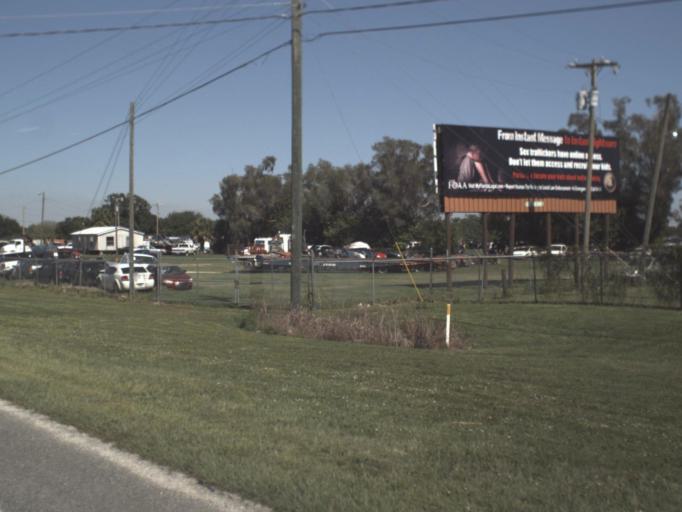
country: US
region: Florida
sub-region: Glades County
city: Moore Haven
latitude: 26.8244
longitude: -81.0823
